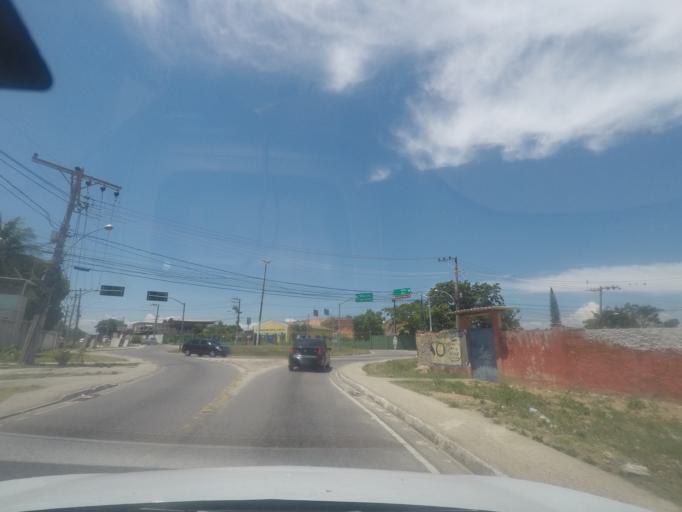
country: BR
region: Rio de Janeiro
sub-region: Itaguai
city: Itaguai
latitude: -22.9781
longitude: -43.6805
